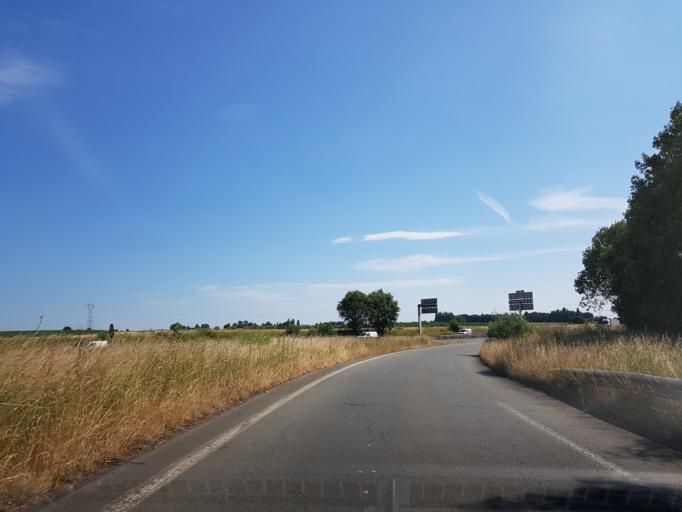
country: FR
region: Nord-Pas-de-Calais
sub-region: Departement du Nord
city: Onnaing
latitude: 50.3673
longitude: 3.5961
